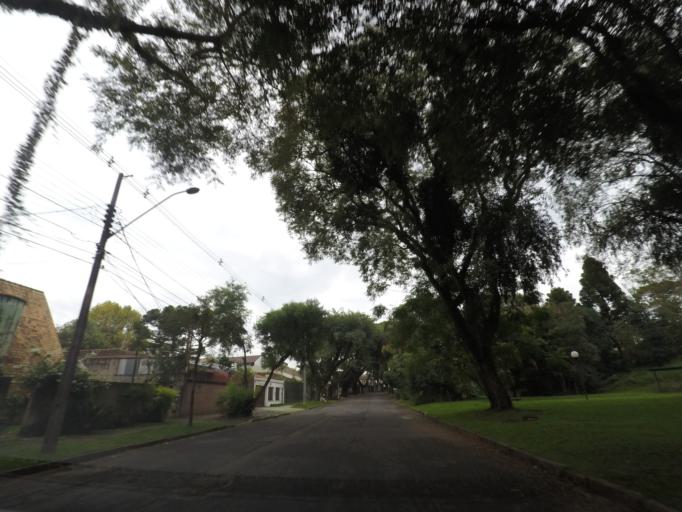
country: BR
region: Parana
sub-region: Curitiba
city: Curitiba
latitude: -25.4514
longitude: -49.3089
